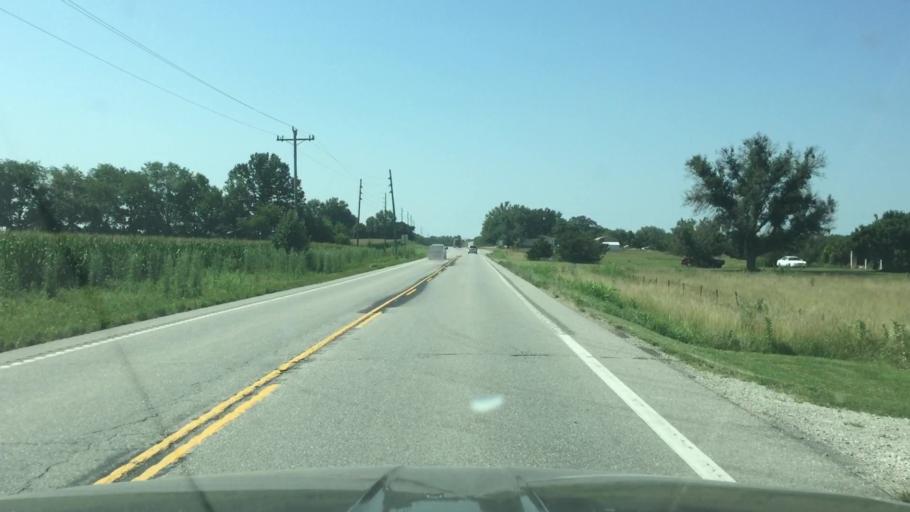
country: US
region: Missouri
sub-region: Moniteau County
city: Tipton
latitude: 38.6389
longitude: -92.7891
